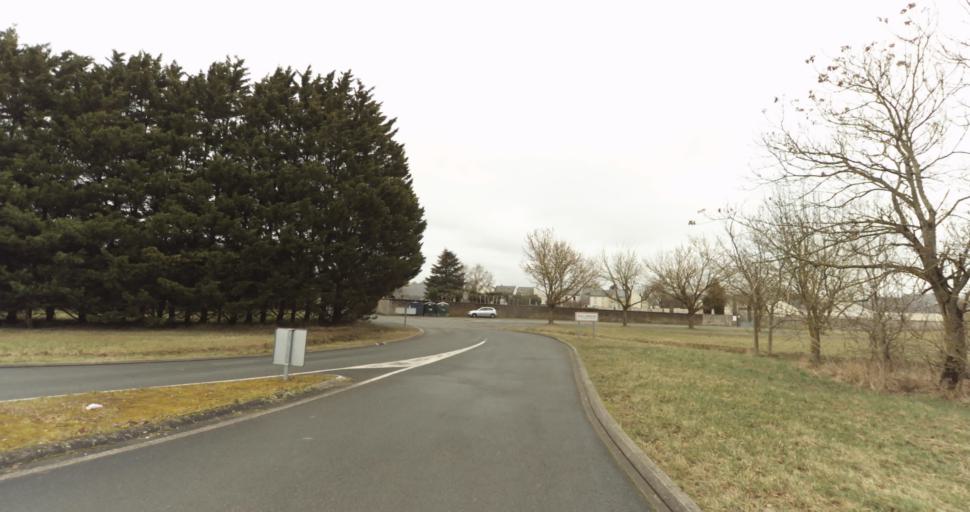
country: FR
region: Pays de la Loire
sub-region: Departement de Maine-et-Loire
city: Doue-la-Fontaine
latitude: 47.1830
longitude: -0.2641
